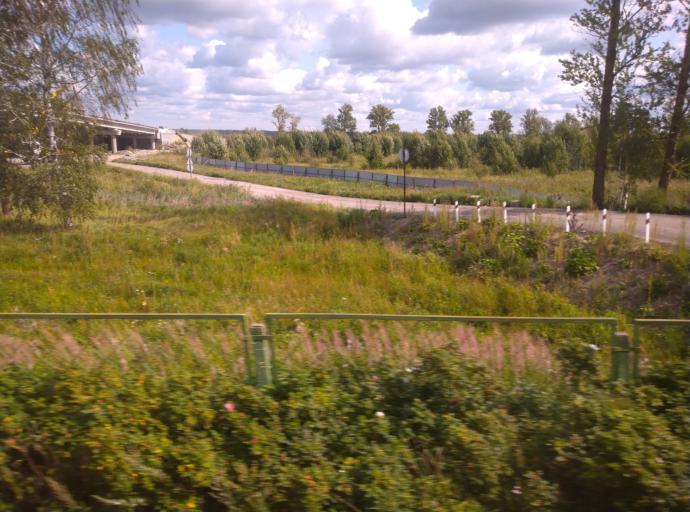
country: RU
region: St.-Petersburg
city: Kolpino
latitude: 59.7330
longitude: 30.6352
